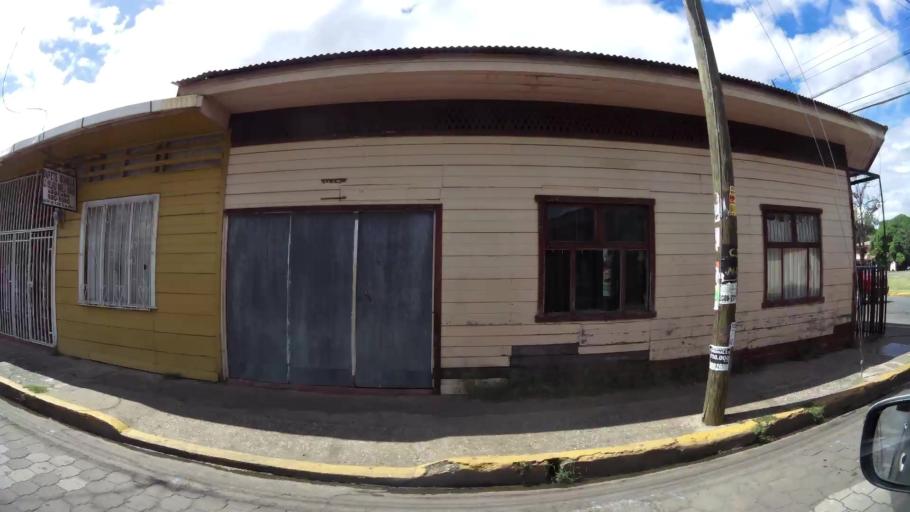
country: CR
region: Guanacaste
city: Santa Cruz
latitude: 10.2624
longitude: -85.5855
